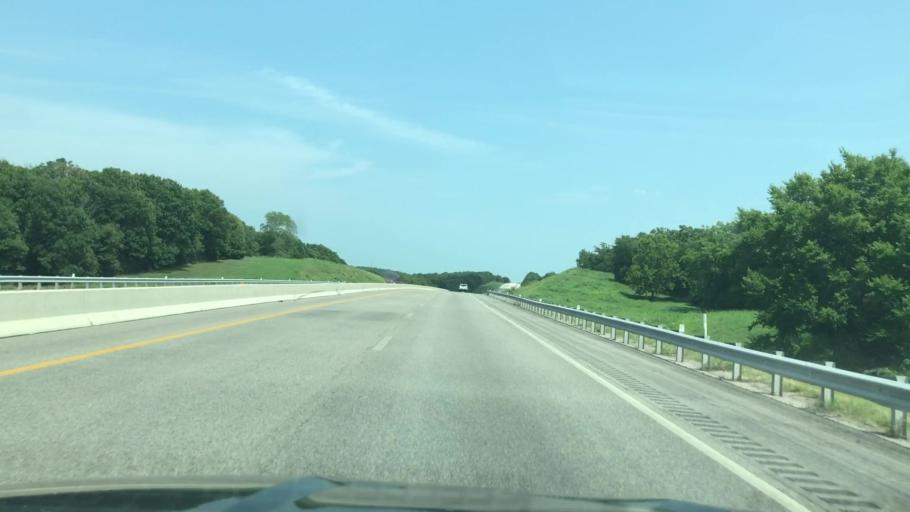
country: US
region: Oklahoma
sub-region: Rogers County
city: Justice
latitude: 36.3372
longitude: -95.5091
